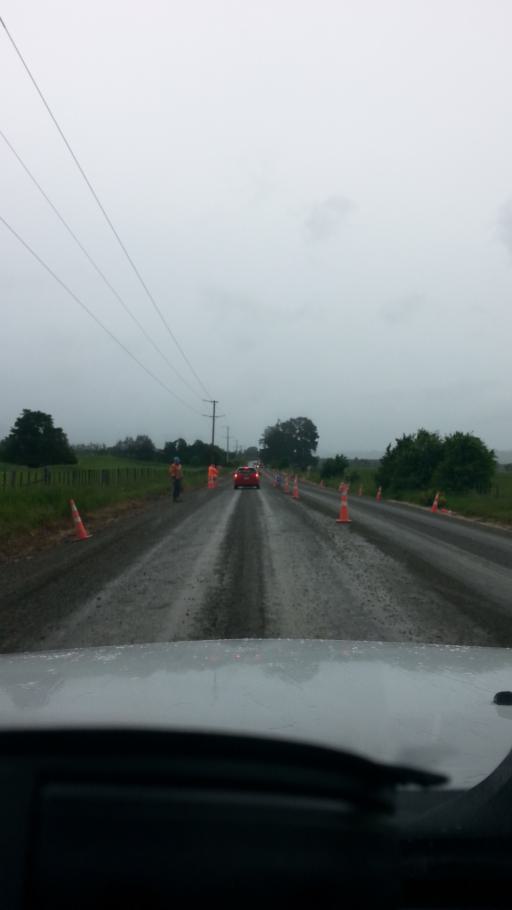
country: NZ
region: Wellington
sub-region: Masterton District
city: Masterton
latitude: -40.8310
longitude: 175.6272
